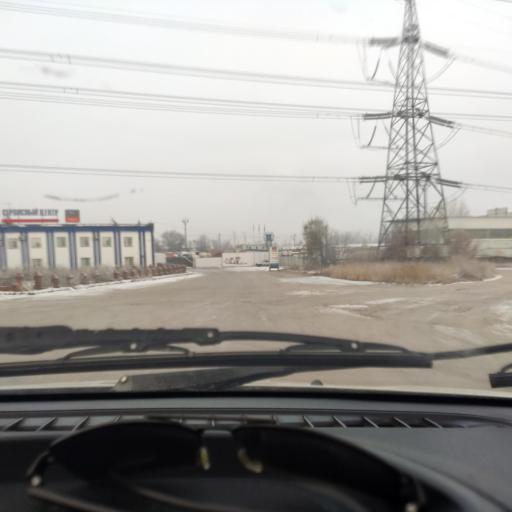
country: RU
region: Samara
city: Zhigulevsk
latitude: 53.4757
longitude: 49.5062
